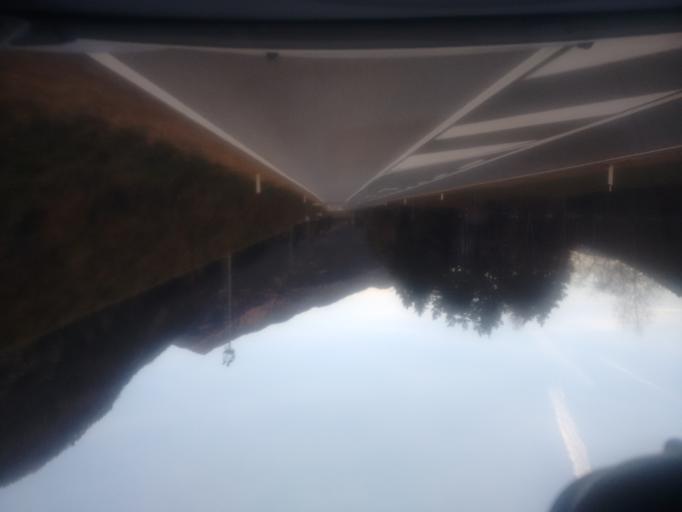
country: IT
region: Trentino-Alto Adige
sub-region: Bolzano
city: Campo di Trens
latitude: 46.8384
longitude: 11.5298
